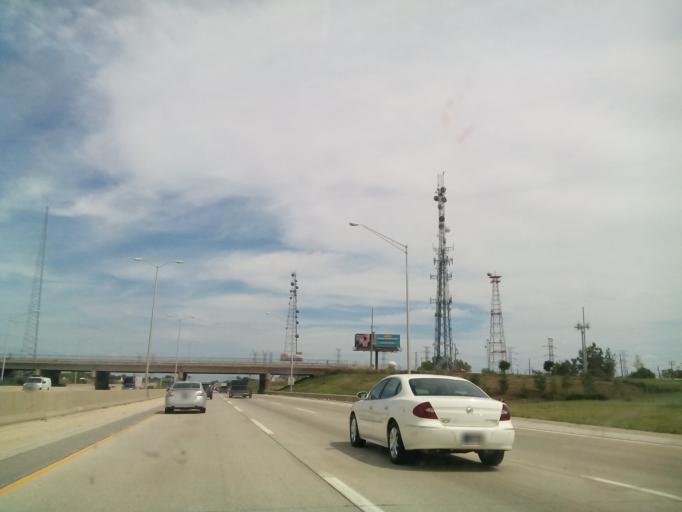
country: US
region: Illinois
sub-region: DuPage County
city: Warrenville
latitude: 41.8008
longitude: -88.2421
